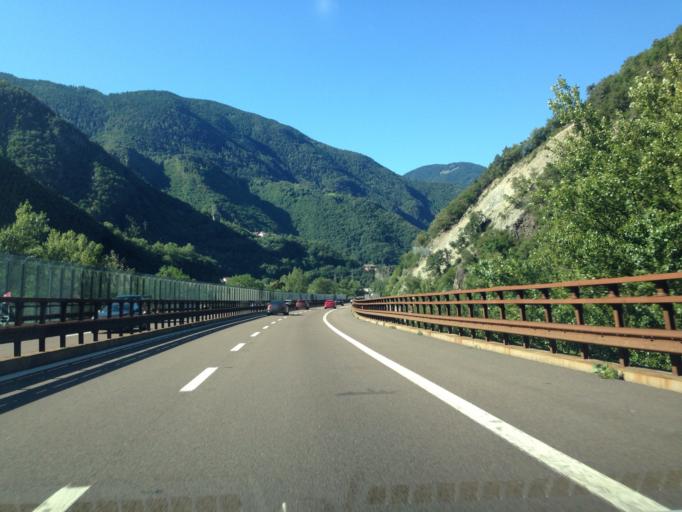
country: IT
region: Trentino-Alto Adige
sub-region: Bolzano
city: Collalbo
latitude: 46.5013
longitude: 11.4539
